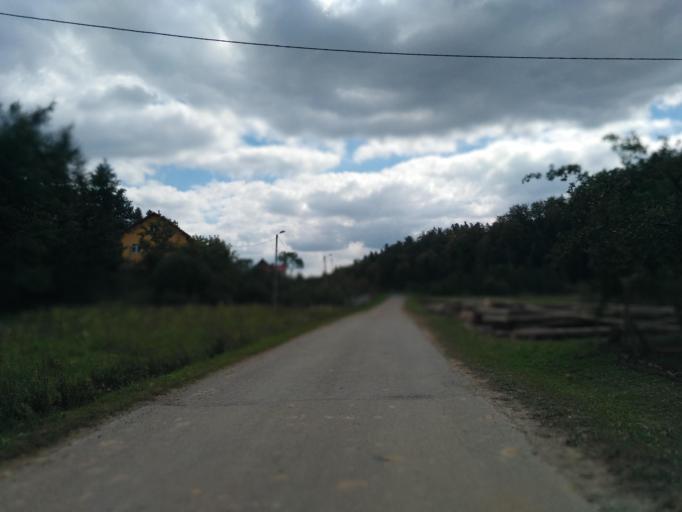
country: PL
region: Subcarpathian Voivodeship
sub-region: Powiat rzeszowski
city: Dynow
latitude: 49.7700
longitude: 22.2618
